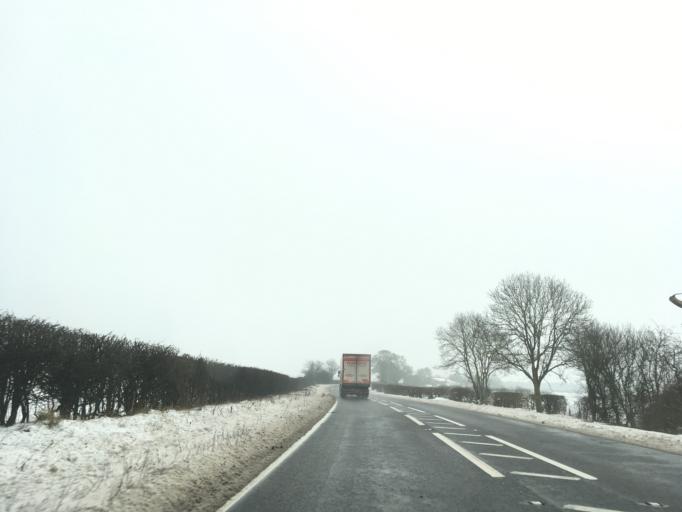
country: GB
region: England
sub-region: Gloucestershire
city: Gotherington
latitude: 52.0192
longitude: -2.0201
